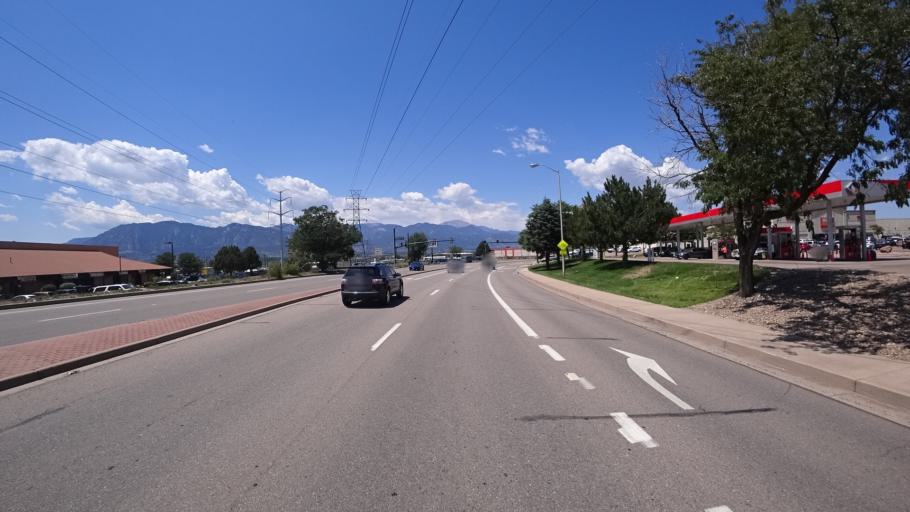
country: US
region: Colorado
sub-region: El Paso County
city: Stratmoor
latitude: 38.7891
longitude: -104.7594
